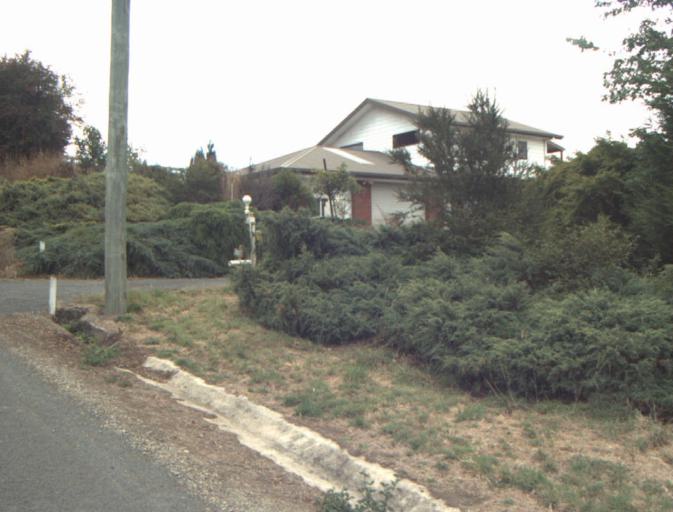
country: AU
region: Tasmania
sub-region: Launceston
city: Mayfield
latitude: -41.2484
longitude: 147.2046
